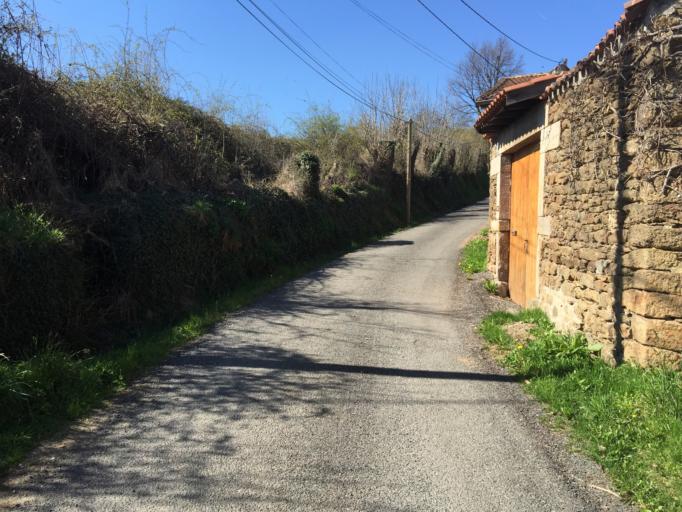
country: FR
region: Rhone-Alpes
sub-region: Departement de la Loire
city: Saint-Chamond
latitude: 45.4868
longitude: 4.4917
